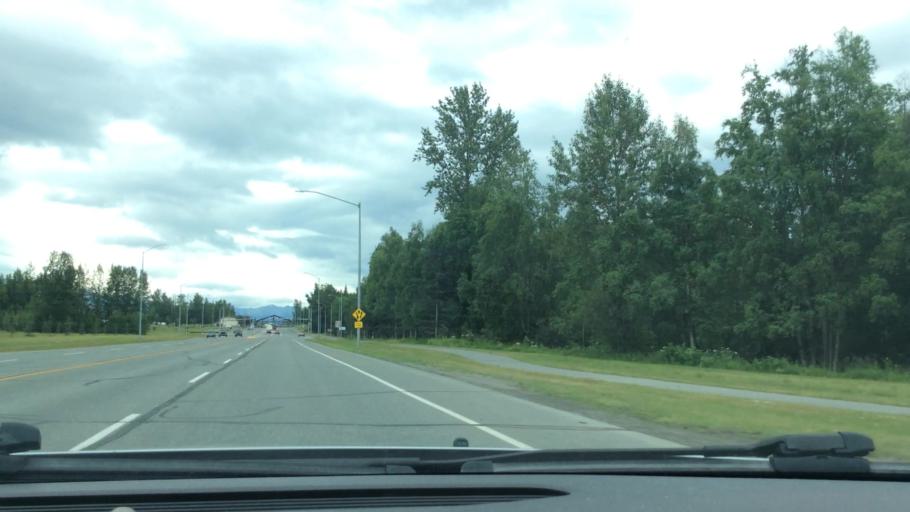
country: US
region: Alaska
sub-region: Anchorage Municipality
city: Anchorage
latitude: 61.2369
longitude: -149.7786
